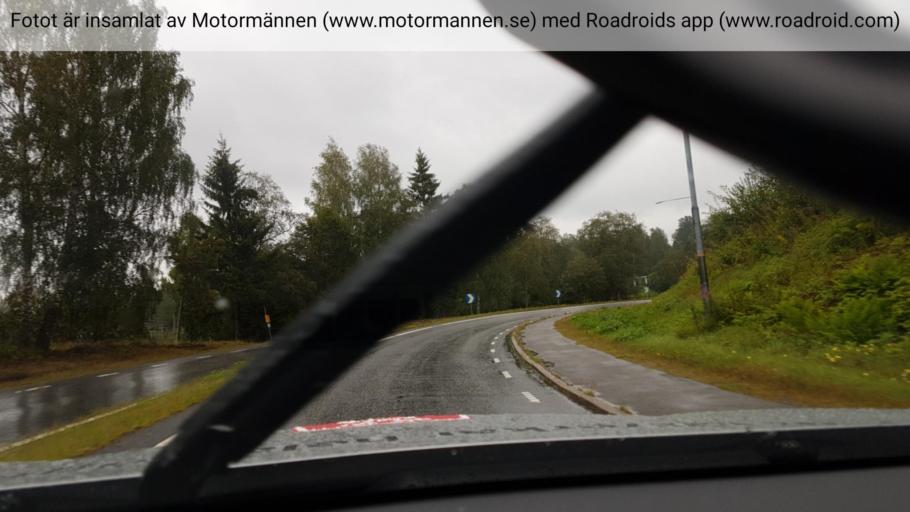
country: SE
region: Vaestra Goetaland
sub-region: Harryda Kommun
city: Hindas
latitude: 57.7077
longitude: 12.4657
